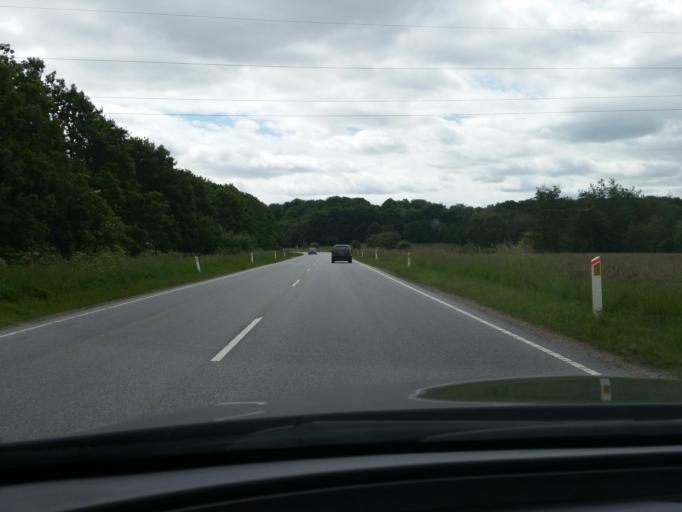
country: DK
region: Central Jutland
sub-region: Horsens Kommune
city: Horsens
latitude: 55.8826
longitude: 9.8252
